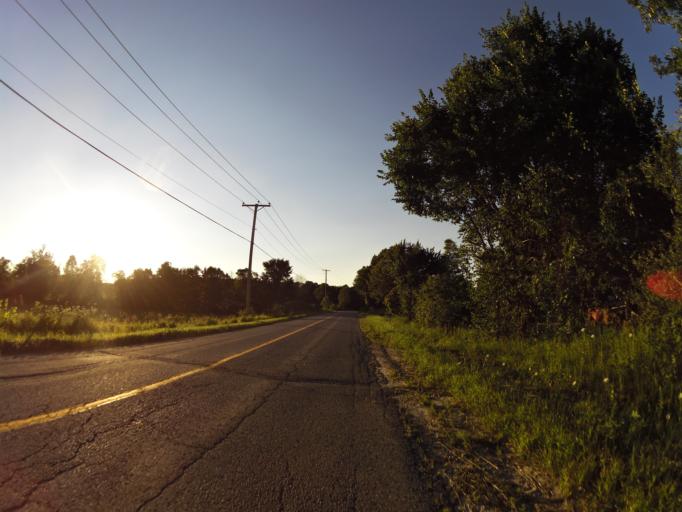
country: CA
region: Quebec
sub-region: Outaouais
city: Wakefield
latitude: 45.6984
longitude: -75.9580
